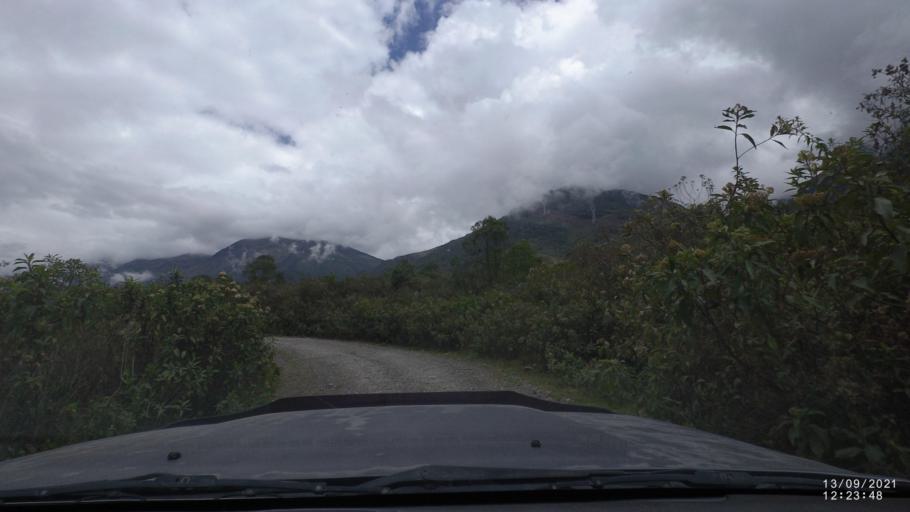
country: BO
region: Cochabamba
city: Colomi
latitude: -17.2438
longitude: -65.8185
